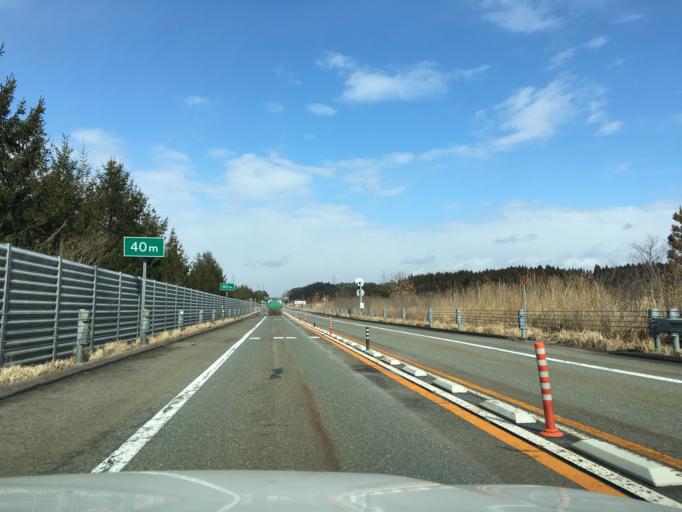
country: JP
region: Akita
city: Akita Shi
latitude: 39.7971
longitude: 140.1002
